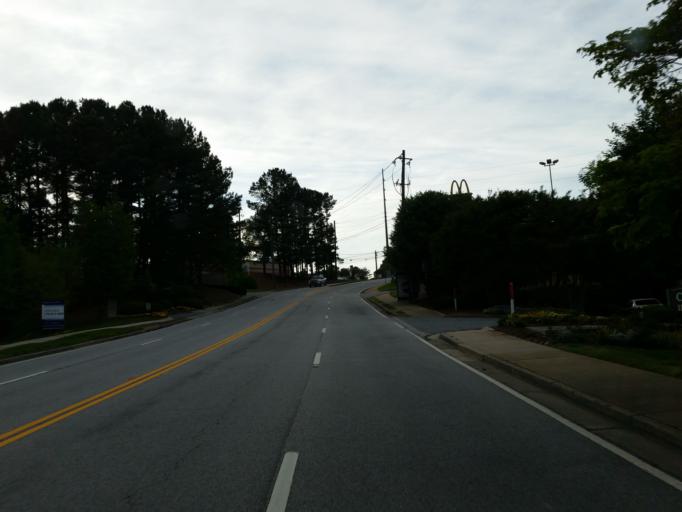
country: US
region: Georgia
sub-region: Cobb County
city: Vinings
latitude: 33.8995
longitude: -84.4742
